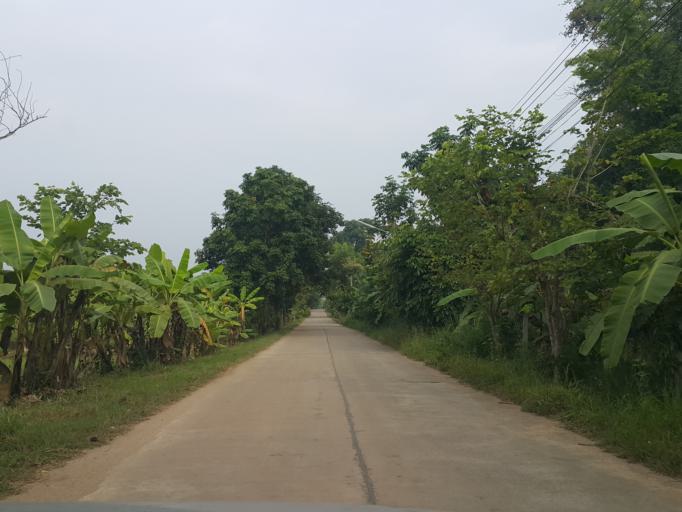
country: TH
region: Mae Hong Son
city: Wiang Nuea
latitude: 19.3703
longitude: 98.4487
